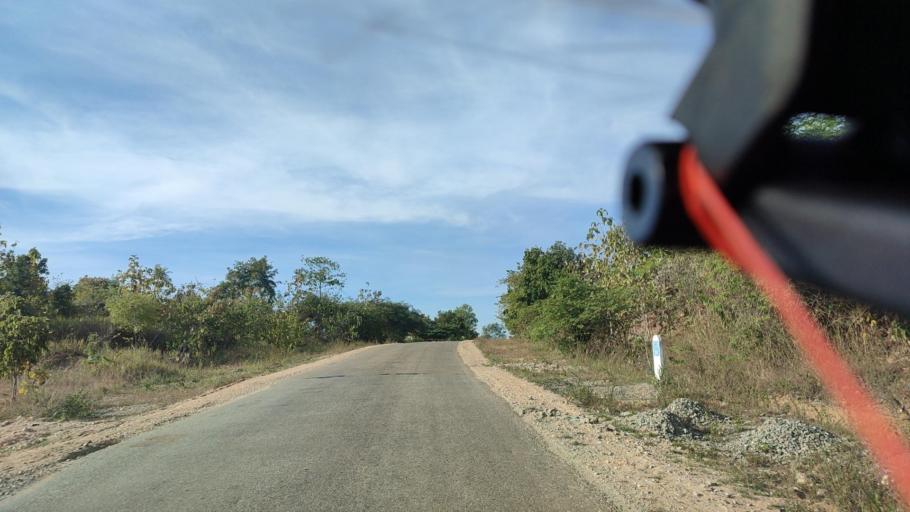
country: MM
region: Mandalay
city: Nay Pyi Taw
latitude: 19.9737
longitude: 95.9800
